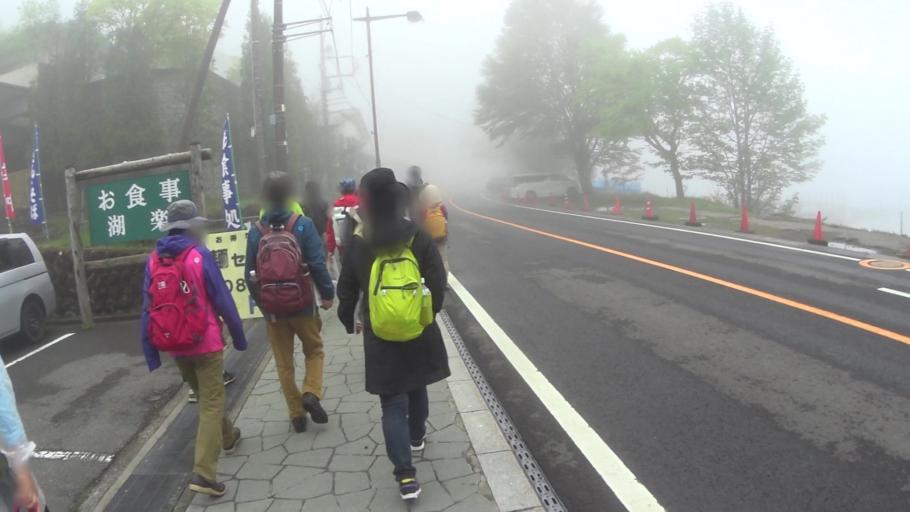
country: JP
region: Tochigi
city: Nikko
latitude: 36.7369
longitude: 139.4961
